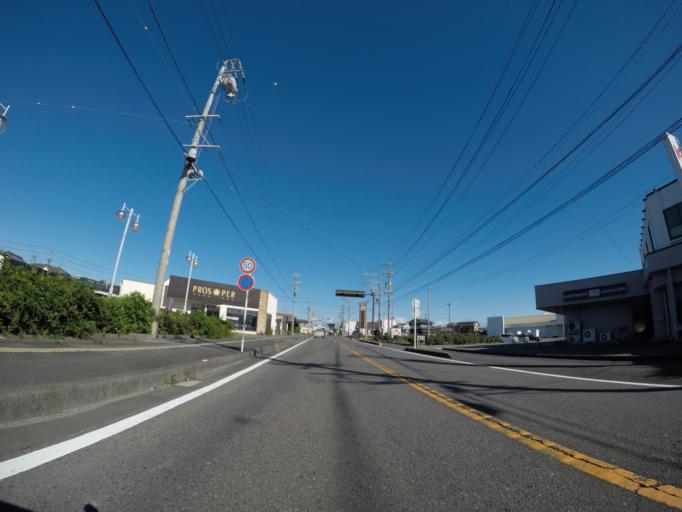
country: JP
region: Shizuoka
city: Sagara
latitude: 34.7488
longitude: 138.2378
